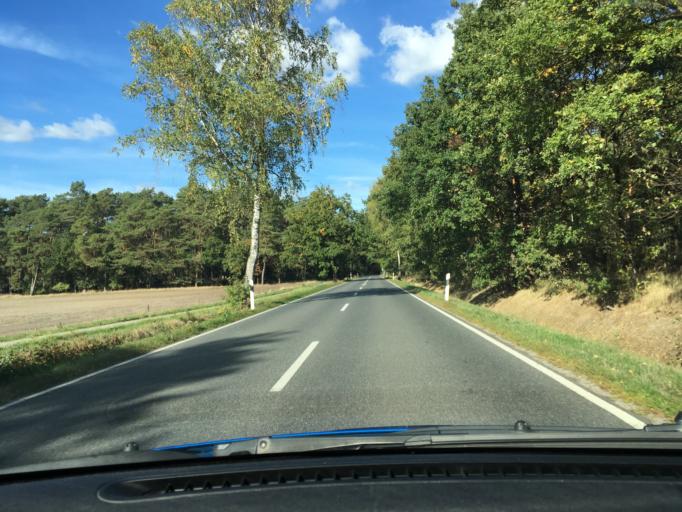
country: DE
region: Lower Saxony
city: Isernhagen Farster Bauerschaft
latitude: 52.5324
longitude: 9.8562
